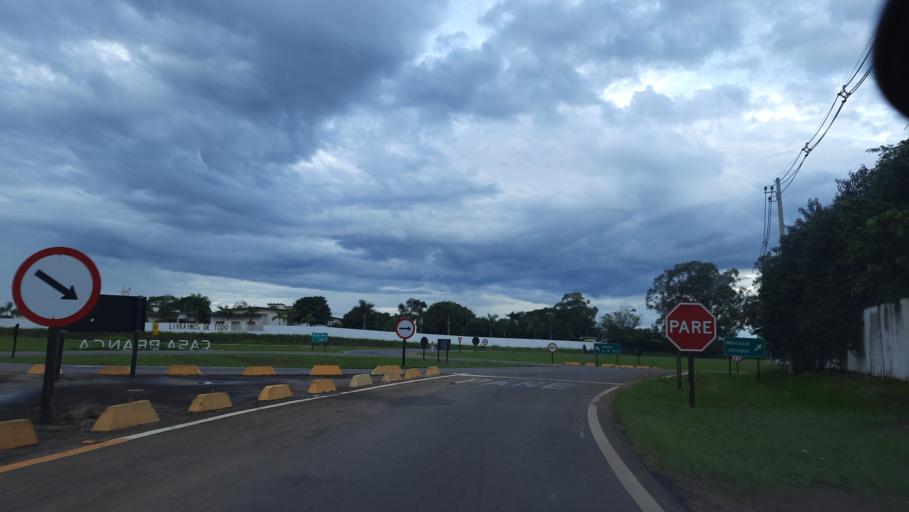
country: BR
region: Sao Paulo
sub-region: Casa Branca
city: Casa Branca
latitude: -21.7702
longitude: -47.0677
